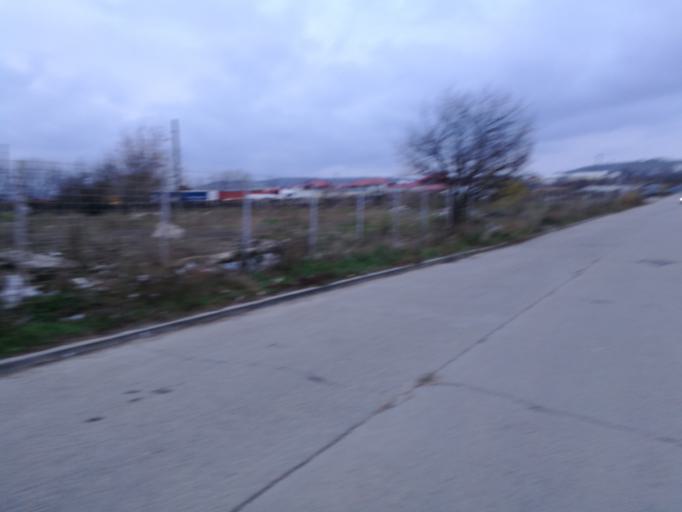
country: RO
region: Suceava
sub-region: Comuna Scheia
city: Scheia
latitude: 47.6665
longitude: 26.2662
